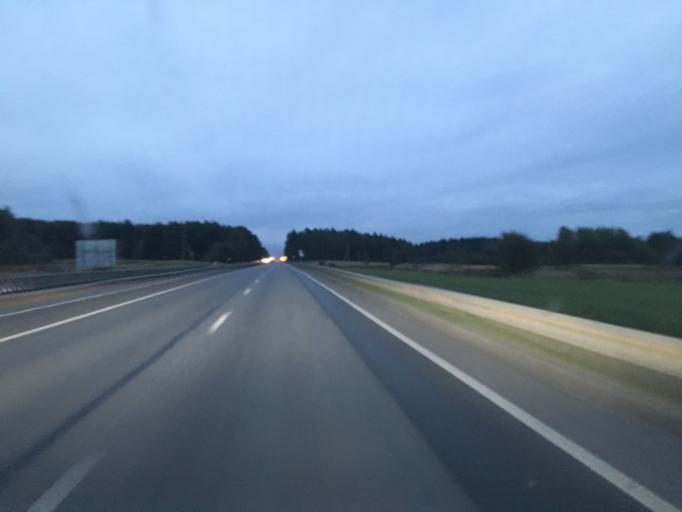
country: RU
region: Kaluga
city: Maloyaroslavets
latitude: 54.9669
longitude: 36.4733
